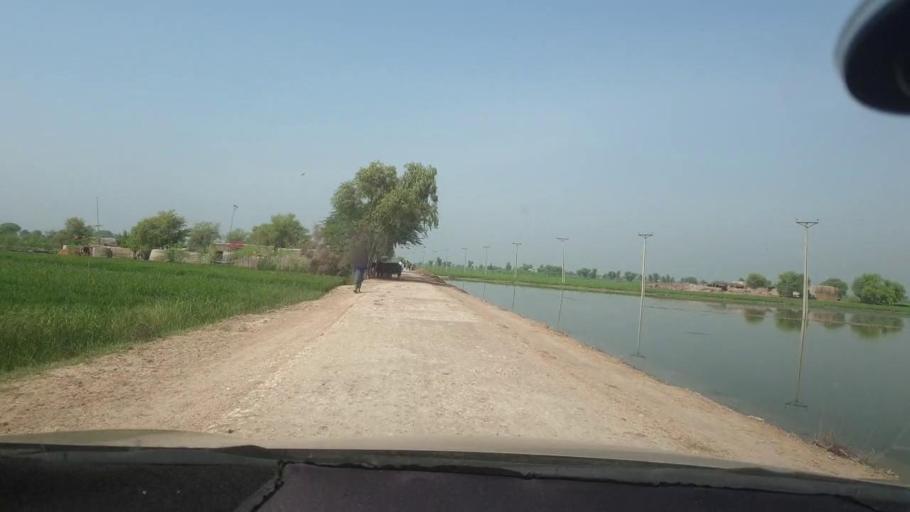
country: PK
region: Sindh
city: Kambar
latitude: 27.6984
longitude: 67.9219
